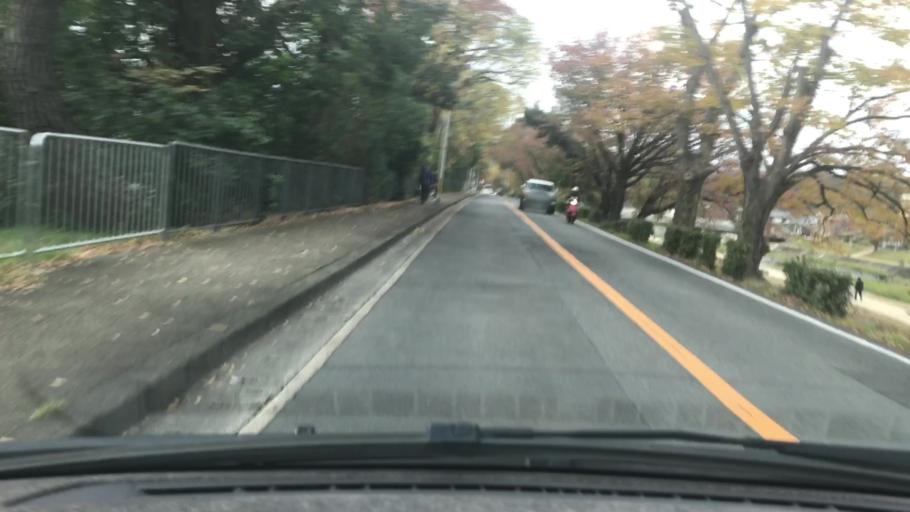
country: JP
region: Kyoto
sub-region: Kyoto-shi
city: Kamigyo-ku
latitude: 35.0478
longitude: 135.7593
